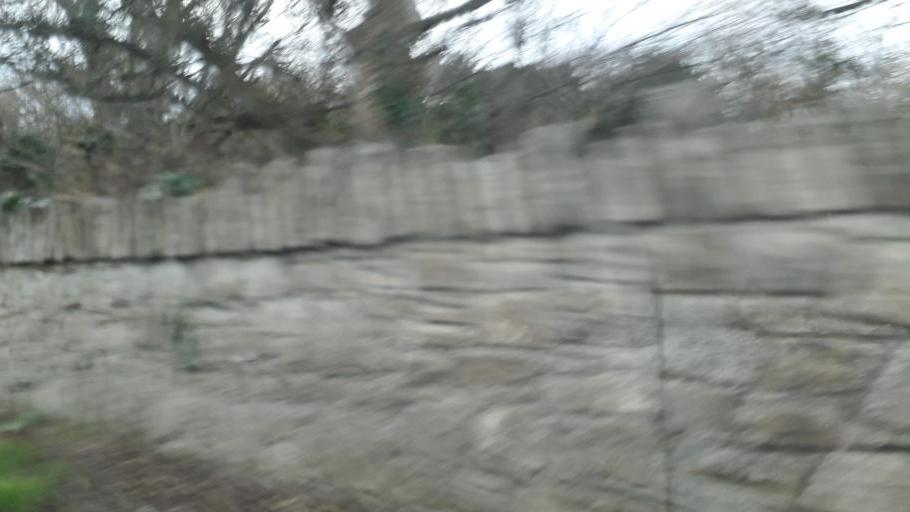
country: IE
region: Leinster
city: An Ros
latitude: 53.5373
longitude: -6.0907
